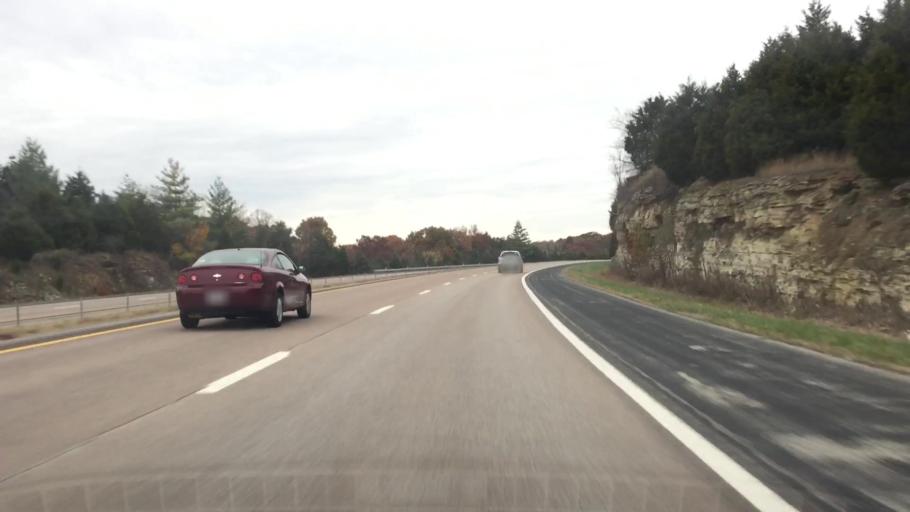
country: US
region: Missouri
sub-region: Boone County
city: Ashland
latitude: 38.6804
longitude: -92.2530
